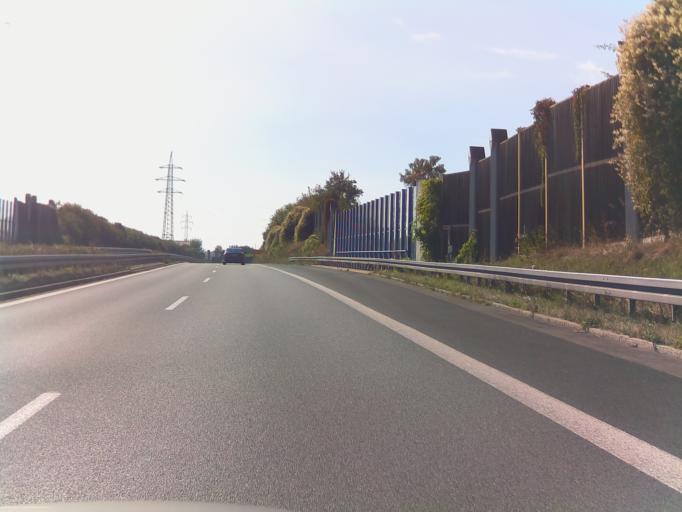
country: DE
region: Bavaria
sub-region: Upper Franconia
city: Lichtenfels
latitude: 50.1374
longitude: 11.0613
